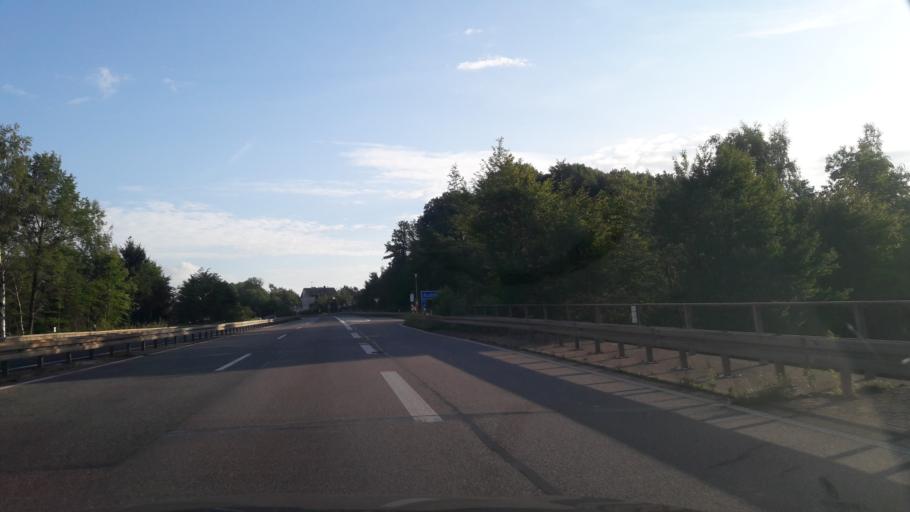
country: DE
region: Saarland
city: Riegelsberg
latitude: 49.2752
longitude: 6.9622
